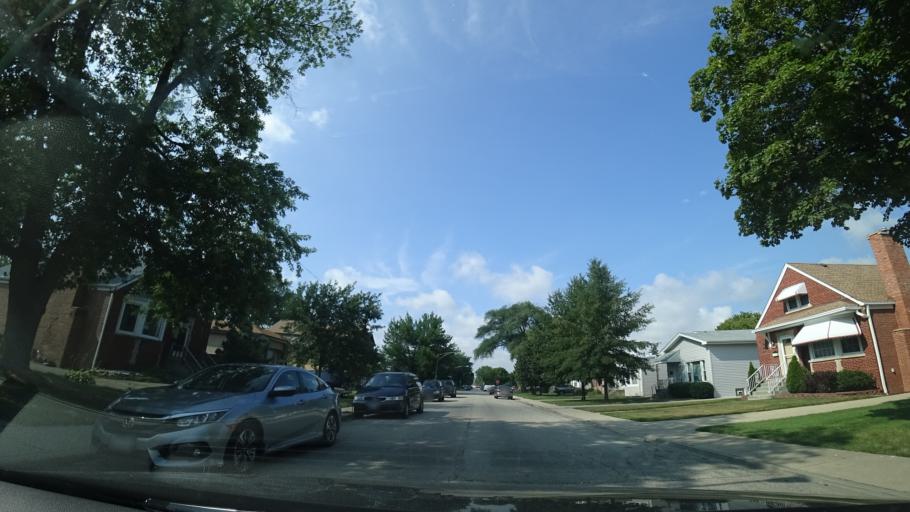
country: US
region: Illinois
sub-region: Cook County
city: Harwood Heights
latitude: 41.9730
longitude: -87.7855
